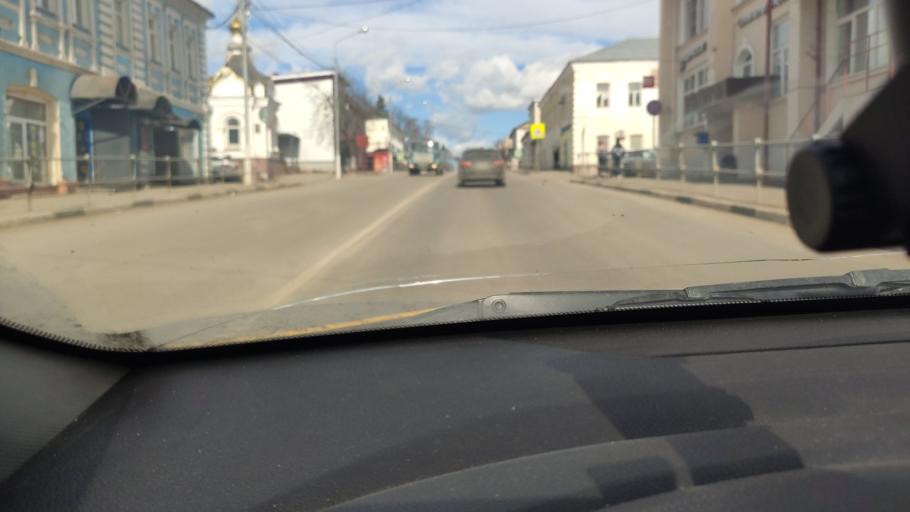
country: RU
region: Moskovskaya
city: Ruza
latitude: 55.7003
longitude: 36.1937
